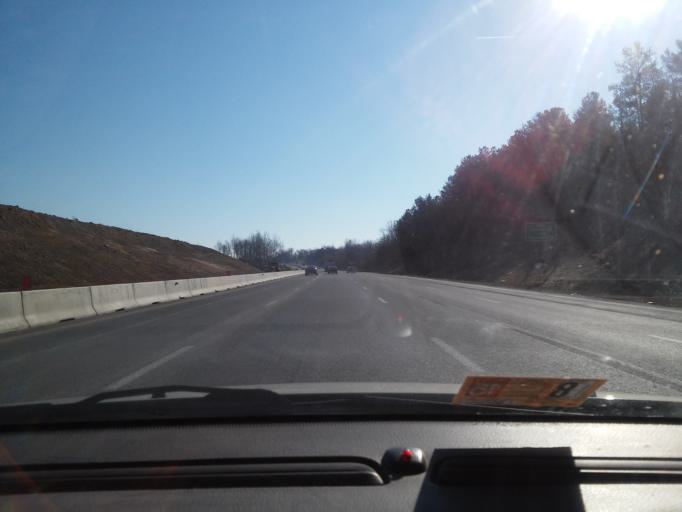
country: US
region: Virginia
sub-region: Henrico County
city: Short Pump
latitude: 37.6690
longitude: -77.6450
